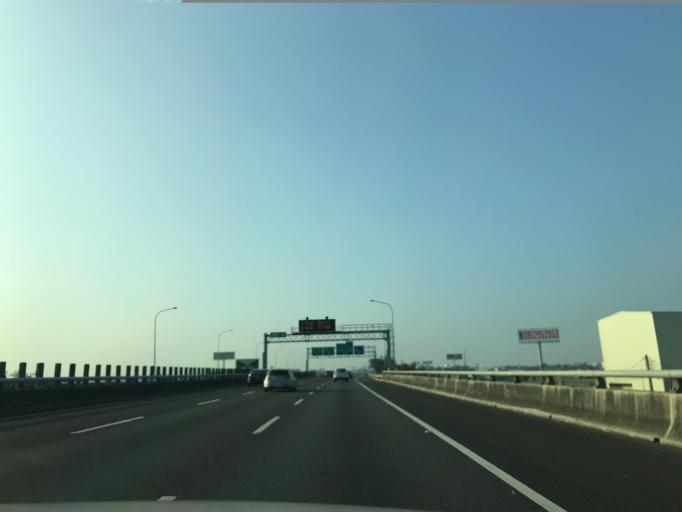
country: TW
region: Taiwan
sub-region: Yunlin
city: Douliu
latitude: 23.7970
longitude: 120.4814
